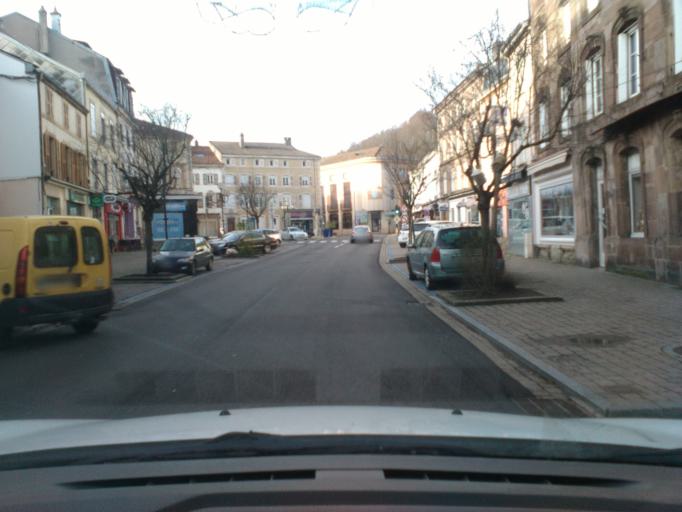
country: FR
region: Lorraine
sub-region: Departement des Vosges
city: Bruyeres
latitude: 48.2102
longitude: 6.7203
